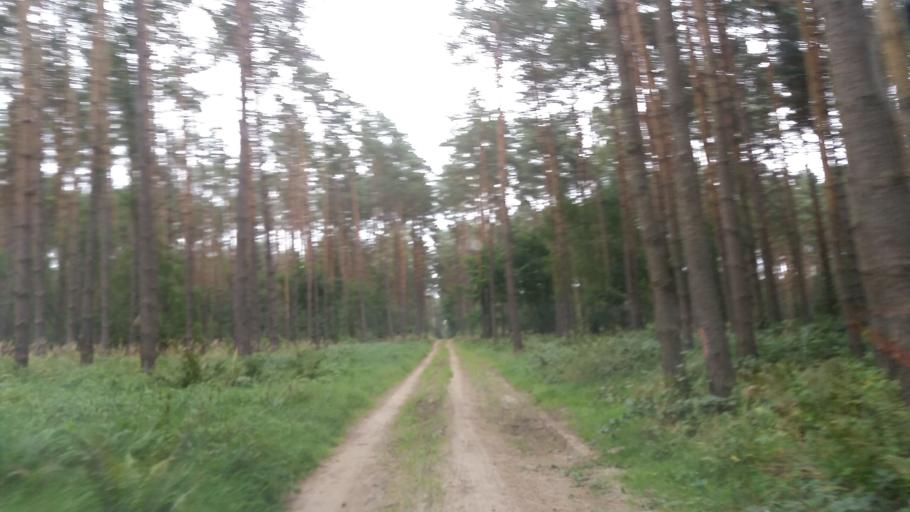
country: PL
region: West Pomeranian Voivodeship
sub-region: Powiat choszczenski
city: Bierzwnik
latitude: 52.9866
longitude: 15.5910
